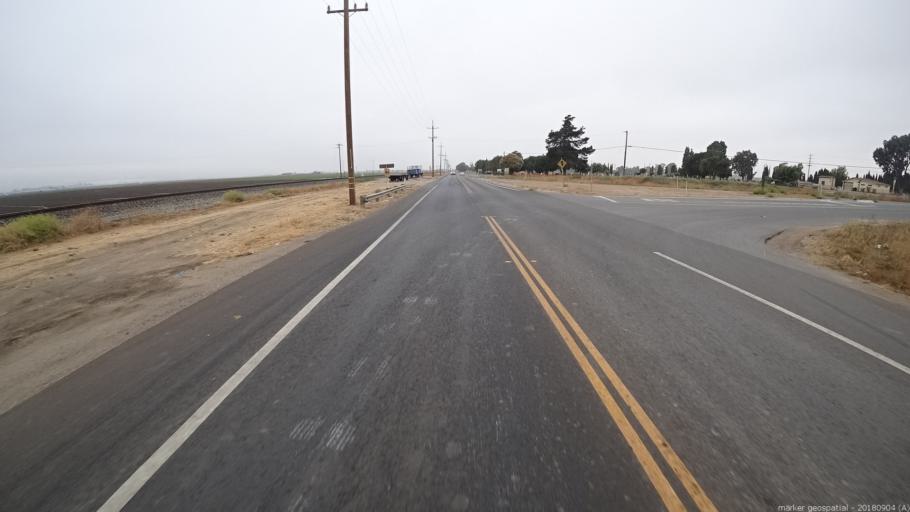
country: US
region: California
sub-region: Monterey County
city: Gonzales
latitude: 36.4929
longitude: -121.4289
